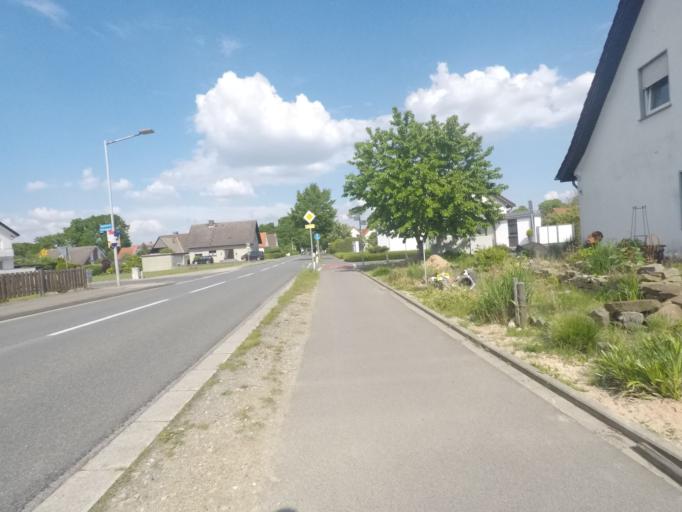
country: DE
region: North Rhine-Westphalia
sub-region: Regierungsbezirk Detmold
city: Kirchlengern
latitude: 52.2201
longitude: 8.6584
